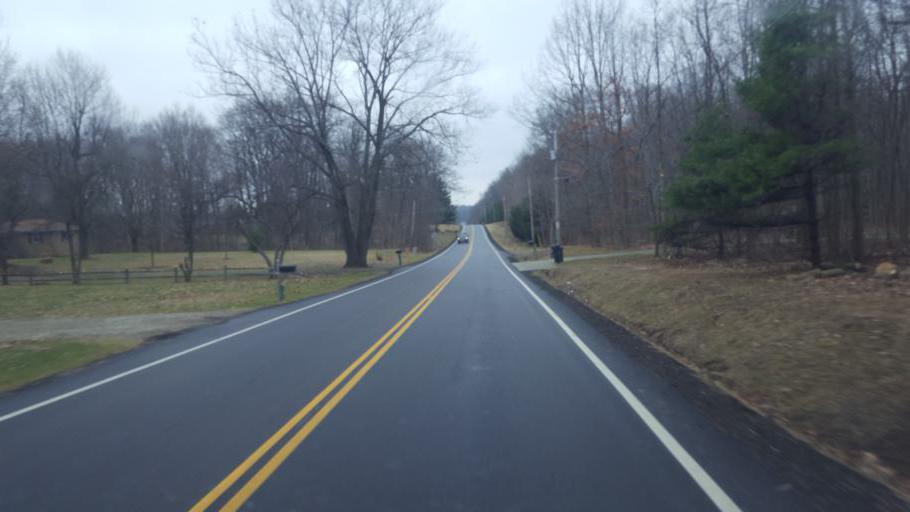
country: US
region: Ohio
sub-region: Richland County
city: Ontario
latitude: 40.7271
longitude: -82.6657
